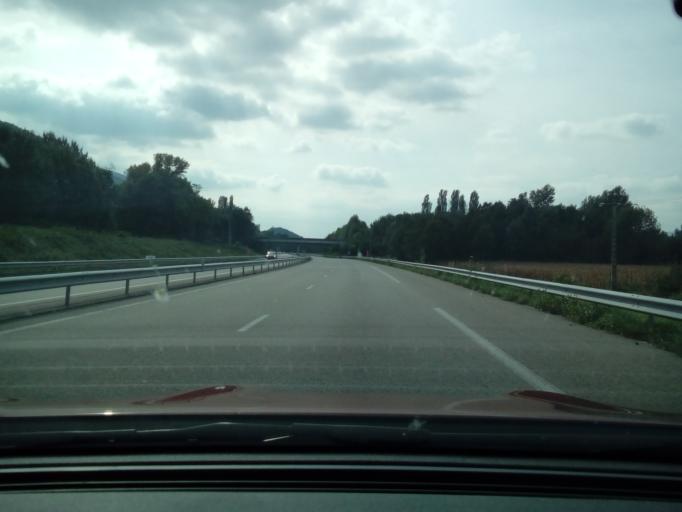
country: FR
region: Rhone-Alpes
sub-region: Departement de l'Isere
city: Veurey-Voroize
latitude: 45.3029
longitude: 5.5897
